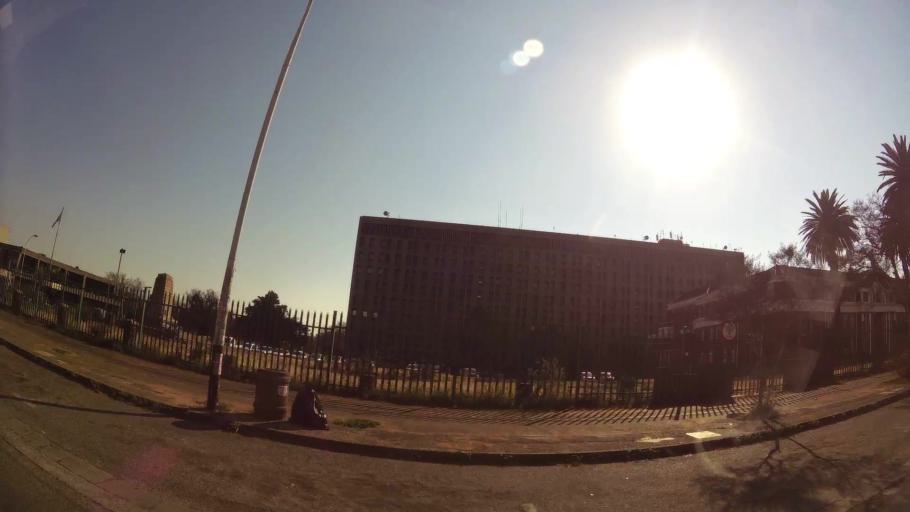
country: ZA
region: Gauteng
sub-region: Ekurhuleni Metropolitan Municipality
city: Boksburg
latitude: -26.2231
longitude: 28.2515
